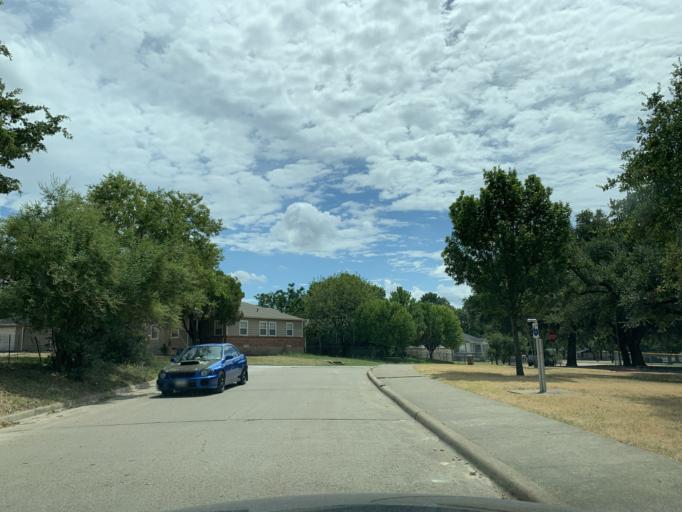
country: US
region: Texas
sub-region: Dallas County
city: Cockrell Hill
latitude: 32.7335
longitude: -96.8762
